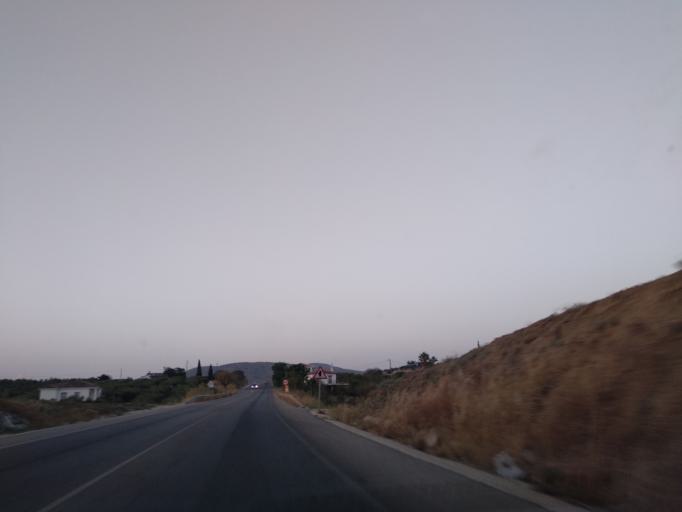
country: ES
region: Andalusia
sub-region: Provincia de Malaga
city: Alhaurin el Grande
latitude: 36.6744
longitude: -4.6625
